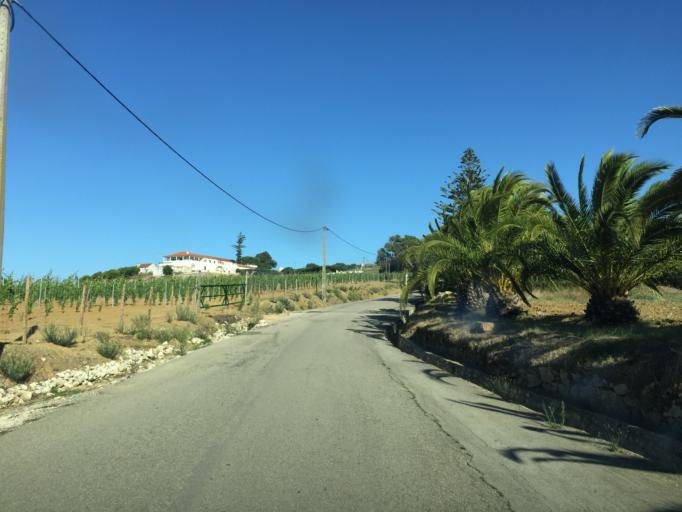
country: PT
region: Lisbon
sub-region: Torres Vedras
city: Torres Vedras
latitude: 39.0944
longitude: -9.2834
